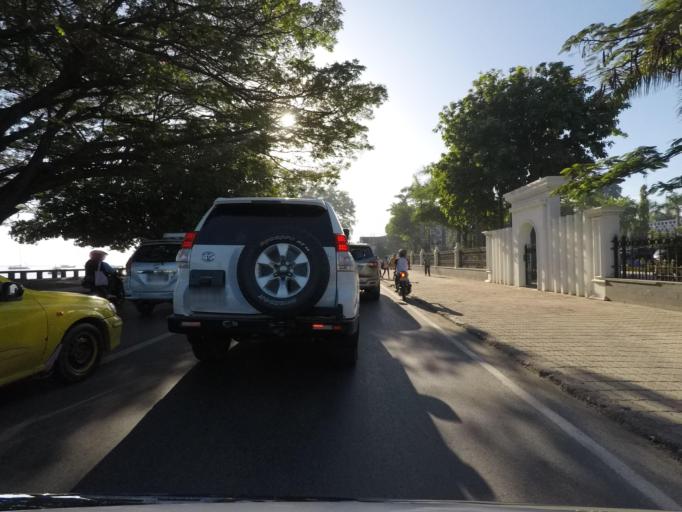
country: TL
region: Dili
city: Dili
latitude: -8.5532
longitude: 125.5786
